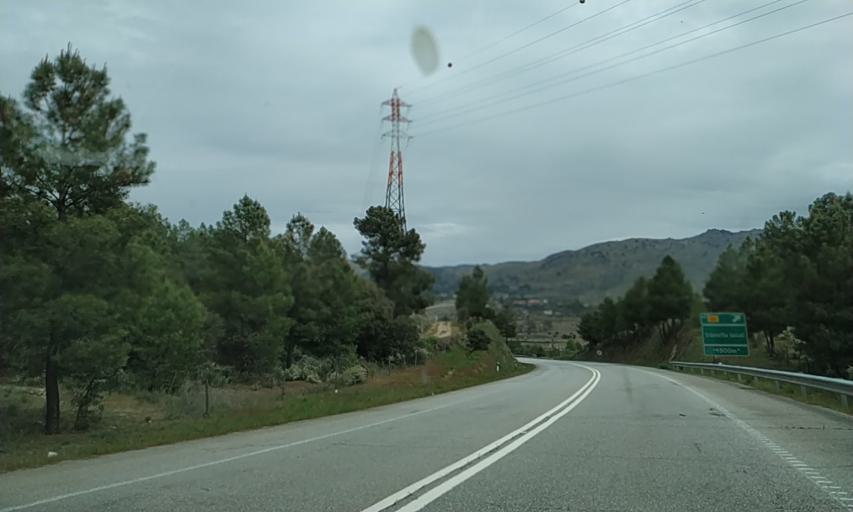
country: PT
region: Guarda
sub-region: Celorico da Beira
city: Celorico da Beira
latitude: 40.6228
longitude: -7.3036
